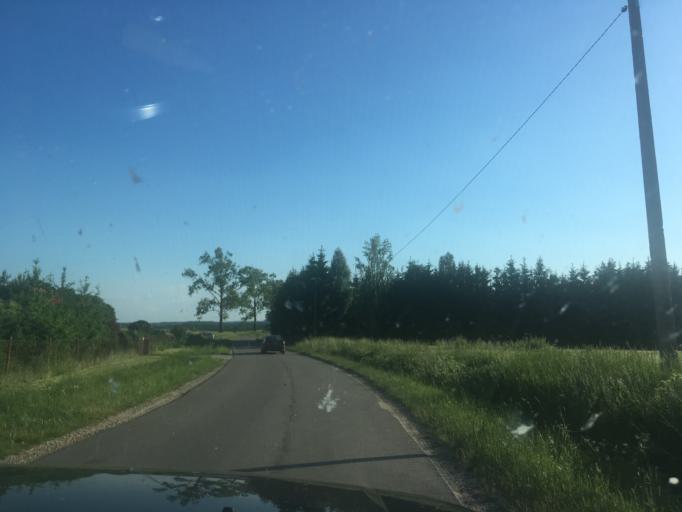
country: PL
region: Warmian-Masurian Voivodeship
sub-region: Powiat ostrodzki
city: Ostroda
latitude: 53.6774
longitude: 20.0423
